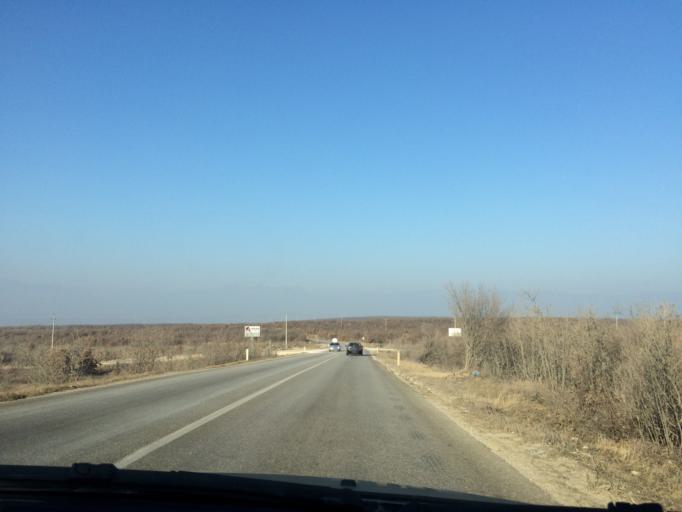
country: XK
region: Pec
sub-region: Komuna e Klines
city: Klina
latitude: 42.5959
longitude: 20.6282
